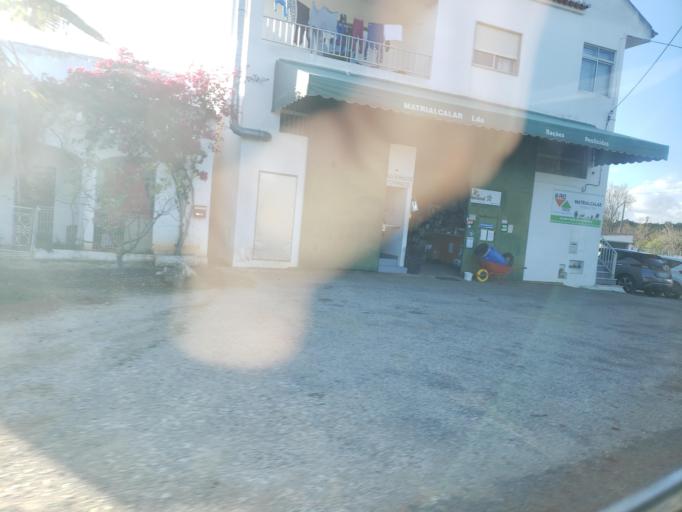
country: PT
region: Faro
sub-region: Portimao
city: Alvor
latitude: 37.1901
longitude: -8.5882
